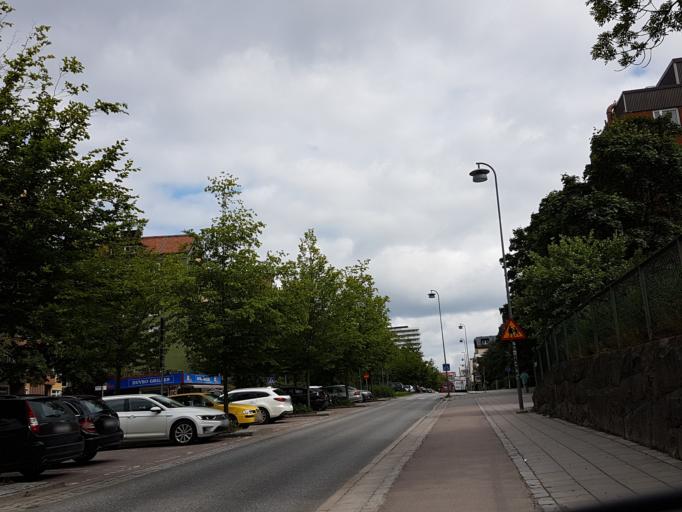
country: SE
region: Stockholm
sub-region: Sundbybergs Kommun
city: Sundbyberg
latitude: 59.3671
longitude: 17.9671
